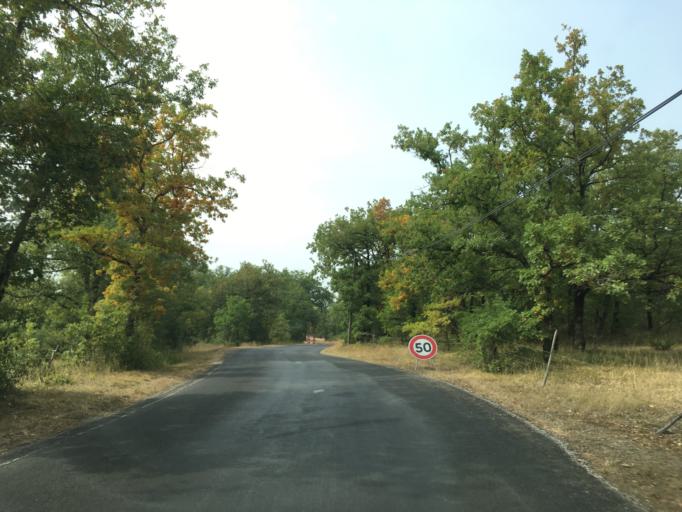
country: FR
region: Midi-Pyrenees
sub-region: Departement du Lot
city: Gramat
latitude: 44.8237
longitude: 1.6003
